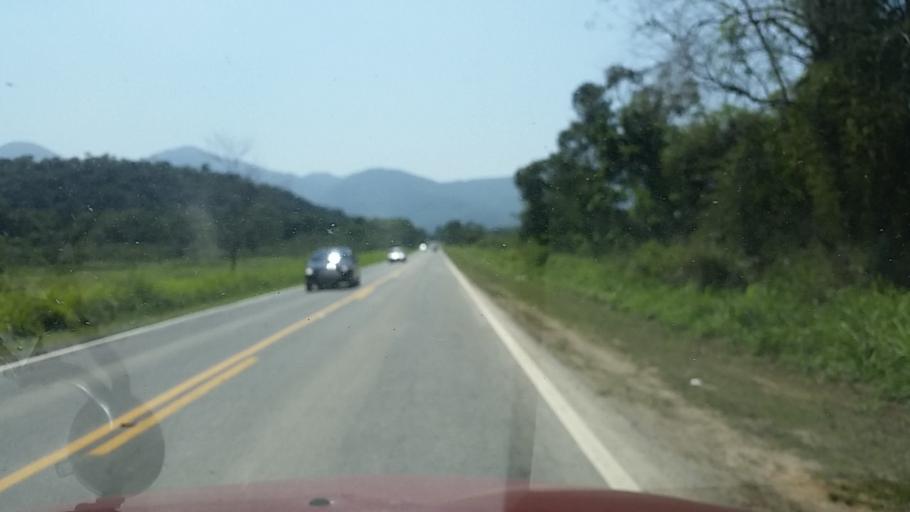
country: BR
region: Sao Paulo
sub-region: Juquia
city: Juquia
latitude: -24.4054
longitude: -47.5316
